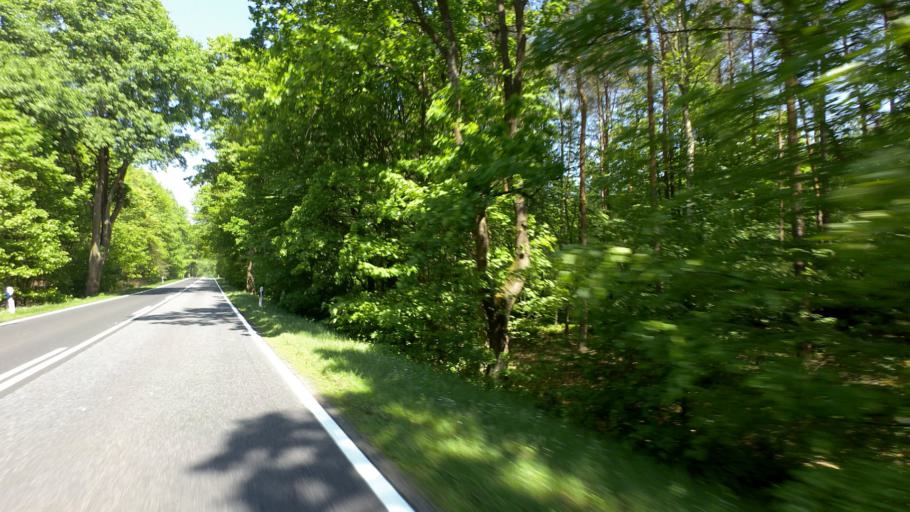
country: DE
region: Brandenburg
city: Grosswoltersdorf
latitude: 53.1027
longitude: 13.1792
